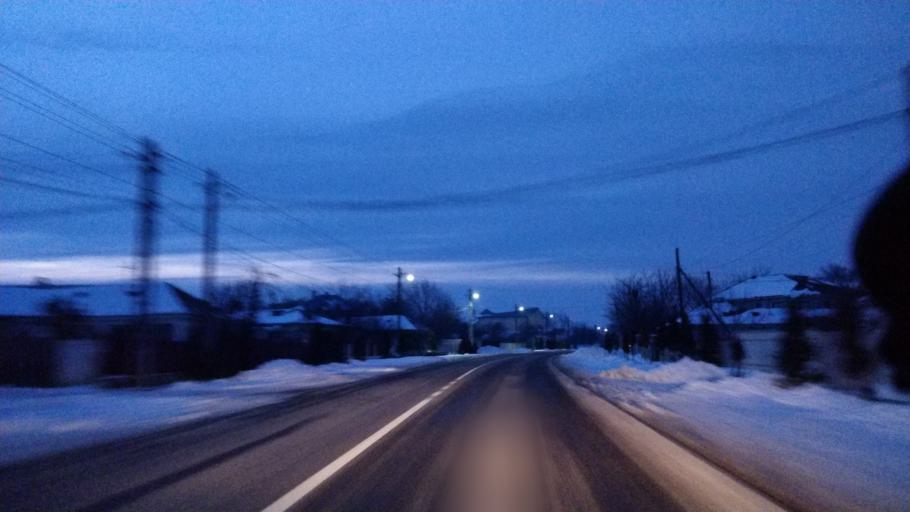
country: RO
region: Vrancea
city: Vulturu de Sus
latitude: 45.6283
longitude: 27.3919
